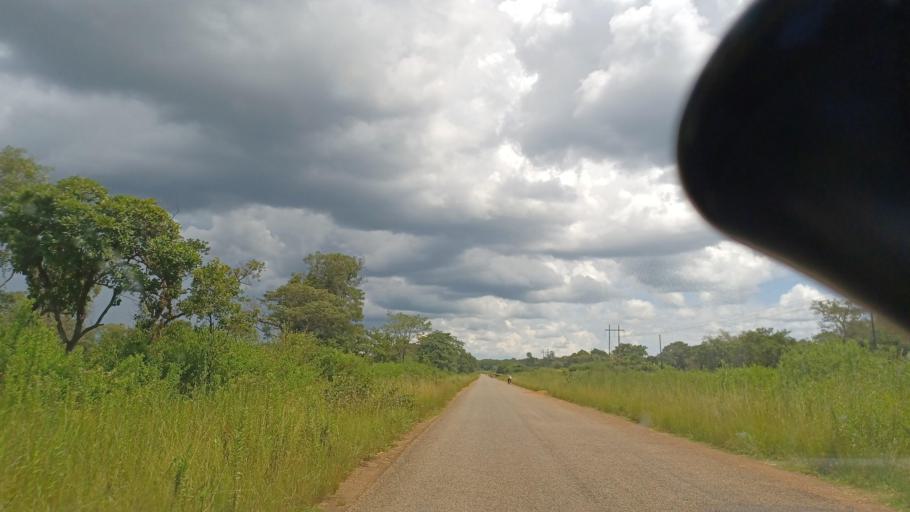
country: ZM
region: North-Western
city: Kasempa
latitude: -12.7732
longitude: 26.0132
